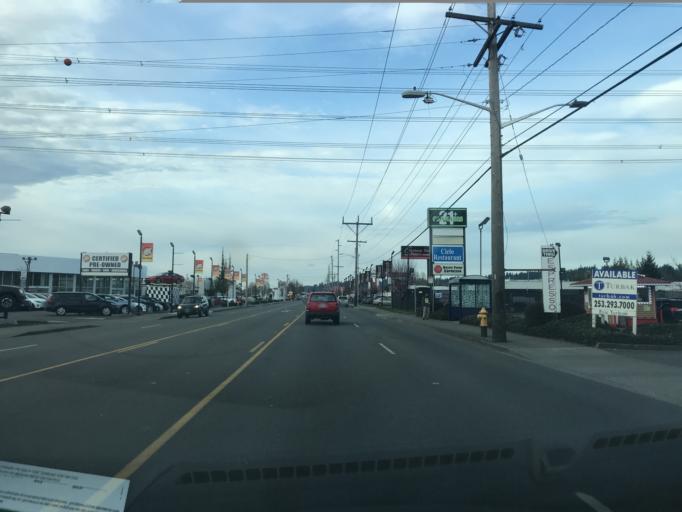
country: US
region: Washington
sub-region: King County
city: Auburn
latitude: 47.3365
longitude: -122.2223
